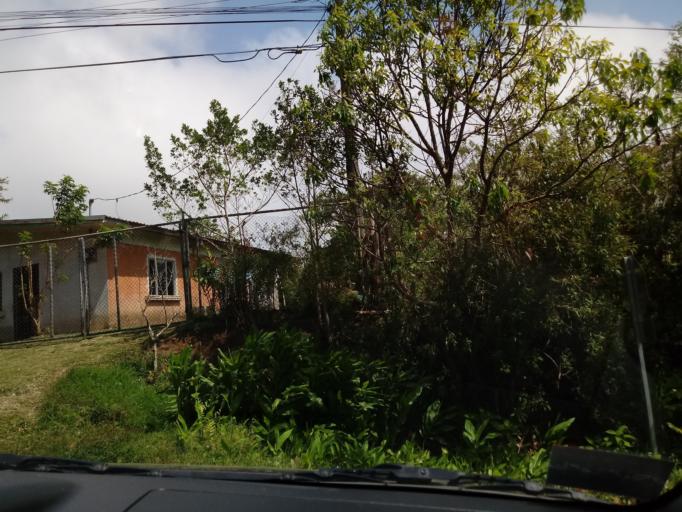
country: CR
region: Heredia
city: Angeles
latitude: 10.0303
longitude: -84.0317
